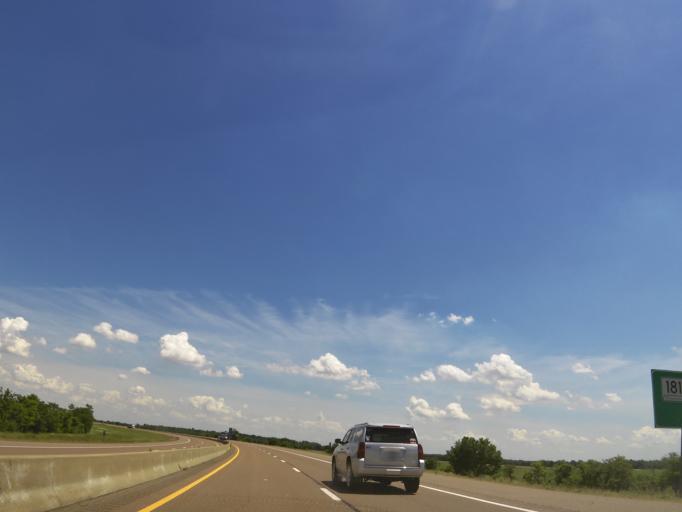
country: US
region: Missouri
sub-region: Pemiscot County
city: Caruthersville
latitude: 36.1009
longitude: -89.6049
